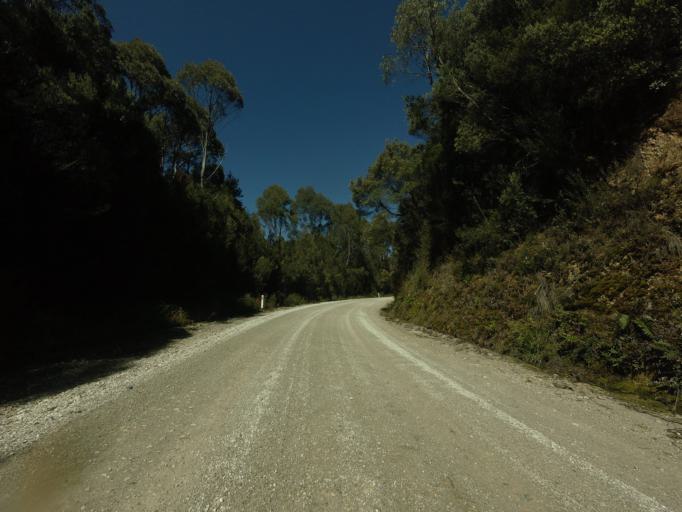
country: AU
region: Tasmania
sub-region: Huon Valley
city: Geeveston
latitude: -42.8281
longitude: 146.3877
